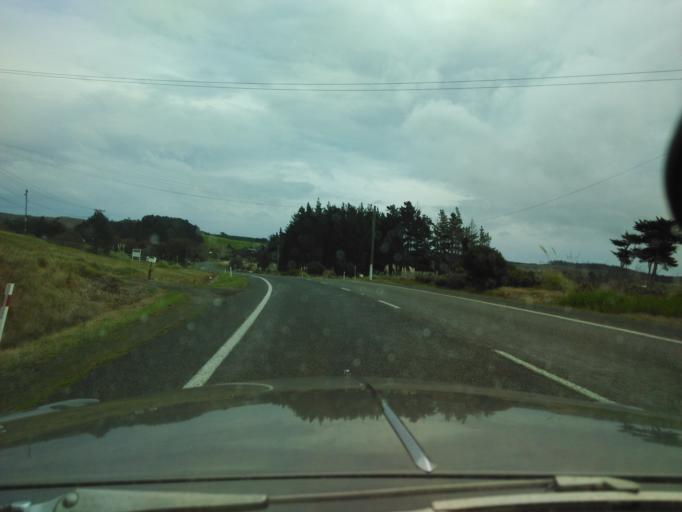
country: NZ
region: Auckland
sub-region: Auckland
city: Muriwai Beach
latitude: -36.7562
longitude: 174.4558
